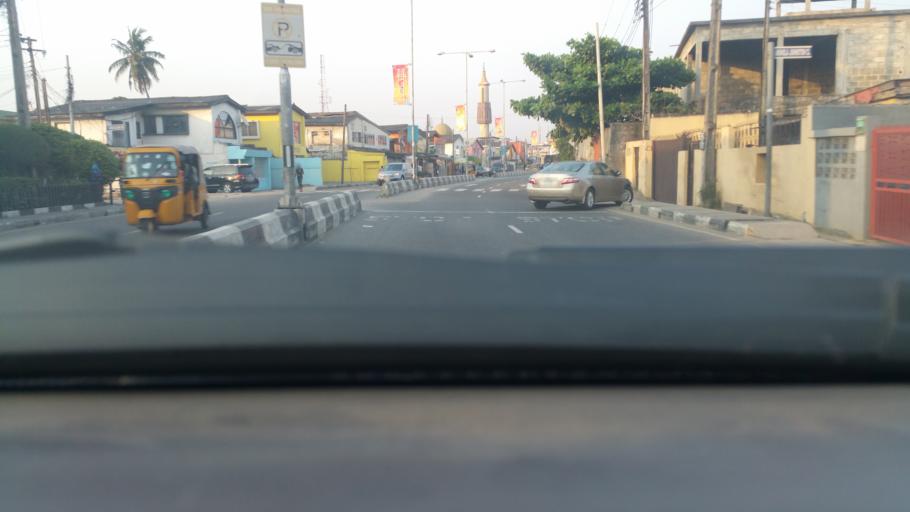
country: NG
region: Lagos
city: Surulere
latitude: 6.4970
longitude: 3.3578
